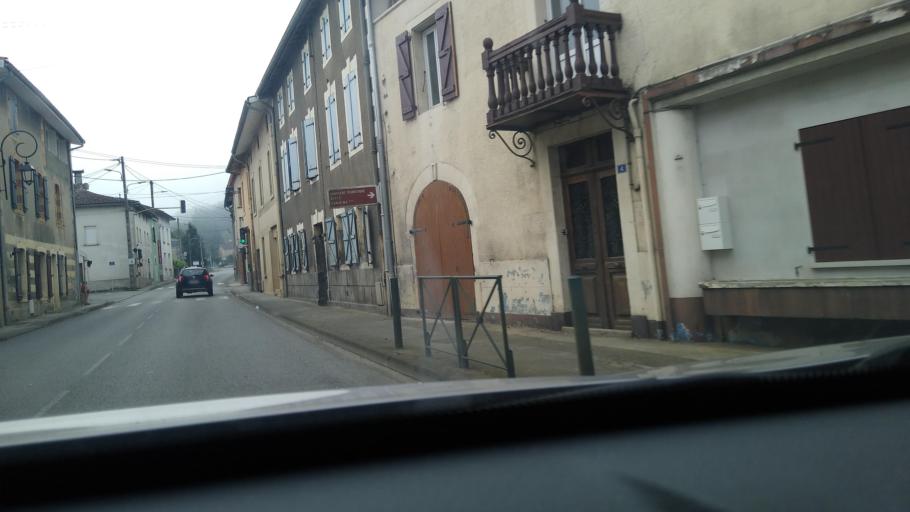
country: FR
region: Midi-Pyrenees
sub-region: Departement de la Haute-Garonne
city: Salies-du-Salat
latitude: 43.0815
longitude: 0.9523
